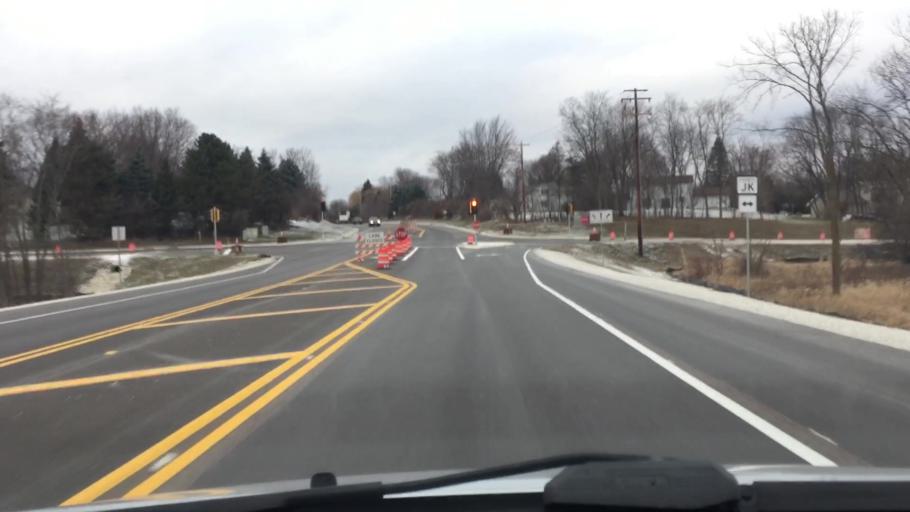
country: US
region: Wisconsin
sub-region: Waukesha County
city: Pewaukee
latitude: 43.1054
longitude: -88.2706
